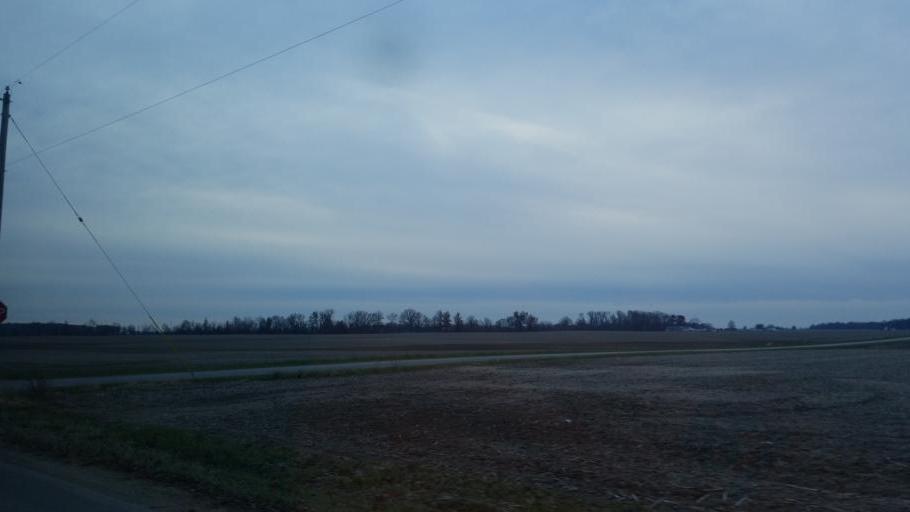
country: US
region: Indiana
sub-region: Adams County
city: Decatur
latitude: 40.7754
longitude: -84.8799
